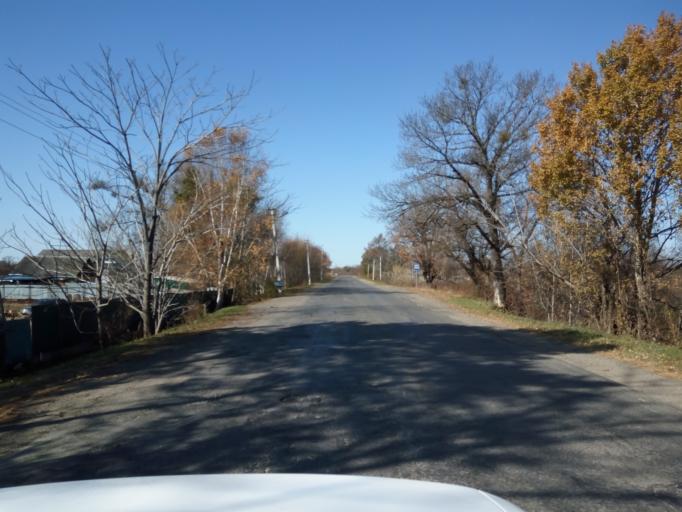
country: RU
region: Primorskiy
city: Dal'nerechensk
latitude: 45.9156
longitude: 133.7859
